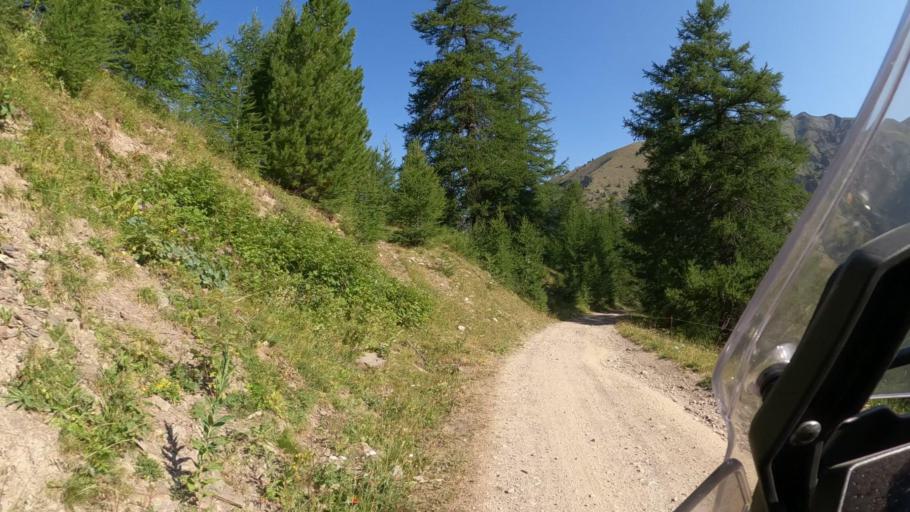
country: FR
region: Provence-Alpes-Cote d'Azur
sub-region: Departement des Hautes-Alpes
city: Guillestre
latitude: 44.5864
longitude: 6.6197
